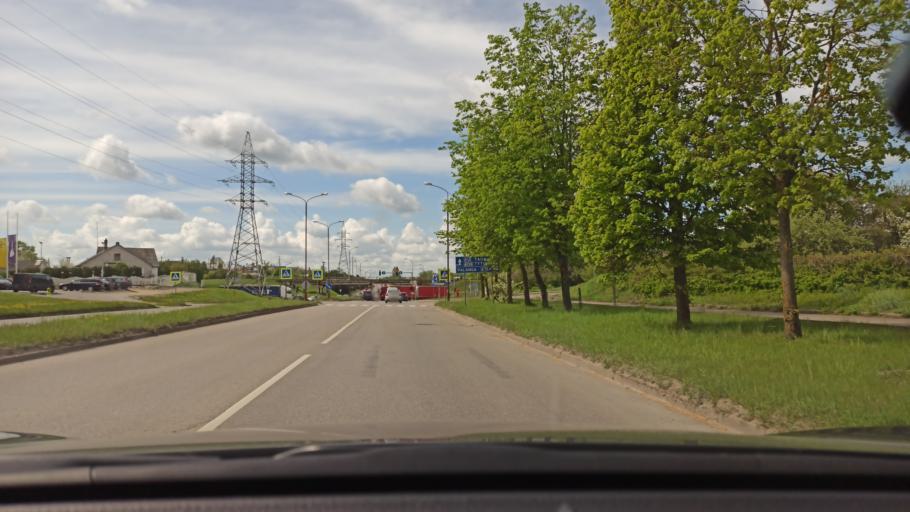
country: LT
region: Siauliu apskritis
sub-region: Siauliai
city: Siauliai
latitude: 55.9164
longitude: 23.3417
